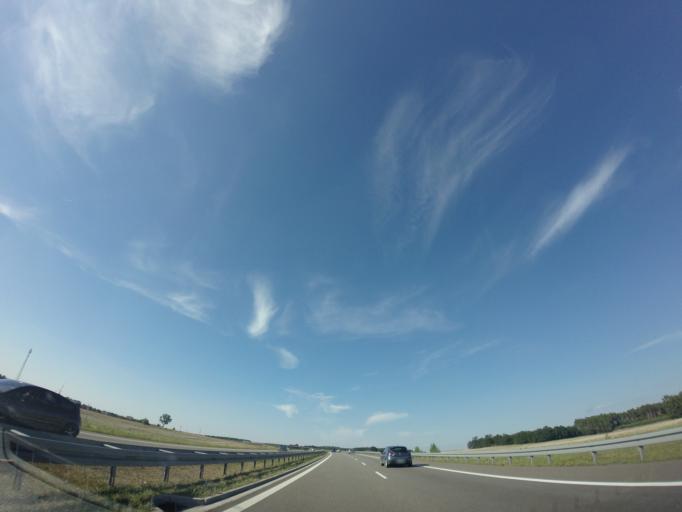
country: PL
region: Lubusz
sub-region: Powiat zielonogorski
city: Sulechow
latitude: 52.1605
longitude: 15.5867
